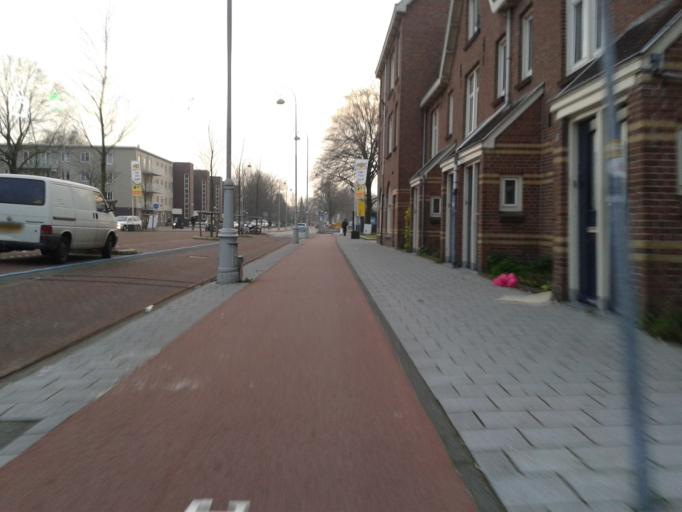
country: NL
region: North Holland
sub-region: Gemeente Amsterdam
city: Amsterdam
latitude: 52.3874
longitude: 4.9085
